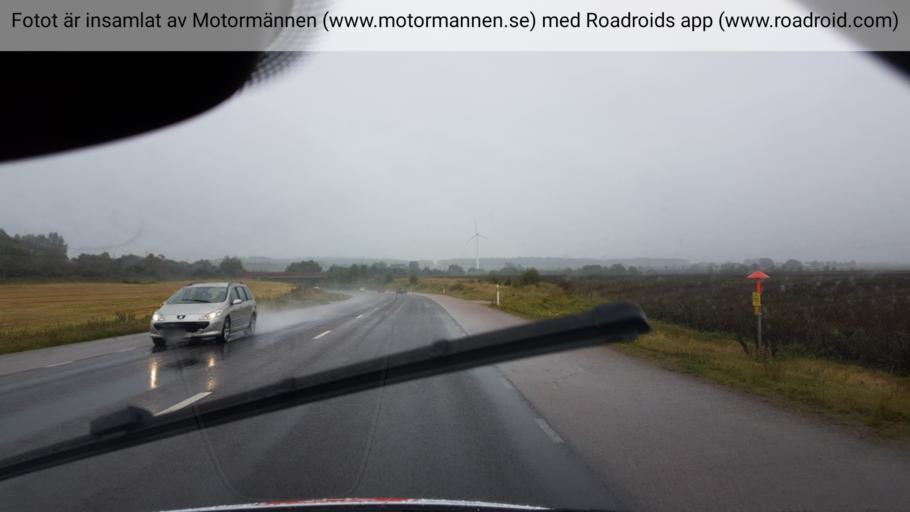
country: SE
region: Halland
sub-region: Laholms Kommun
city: Veinge
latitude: 56.5789
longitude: 13.0066
